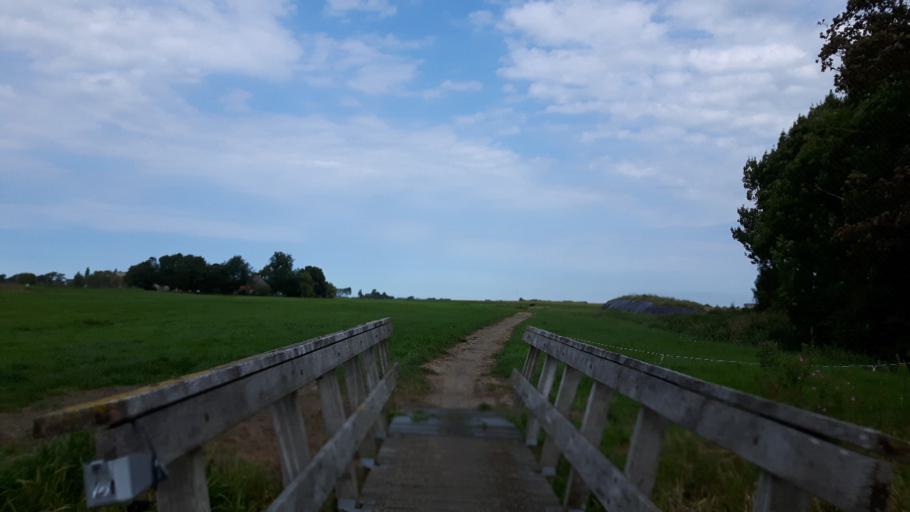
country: NL
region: Friesland
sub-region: Gemeente Leeuwarden
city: Camminghaburen
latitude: 53.2372
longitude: 5.8297
